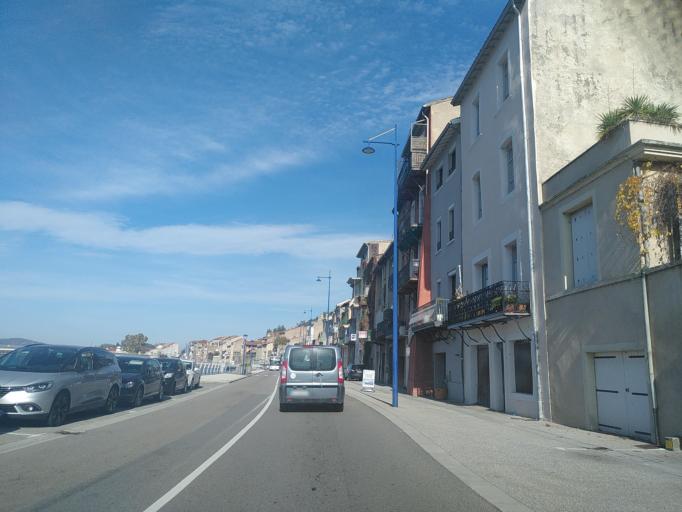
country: FR
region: Rhone-Alpes
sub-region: Departement de la Drome
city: Saint-Vallier
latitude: 45.1790
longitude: 4.8135
